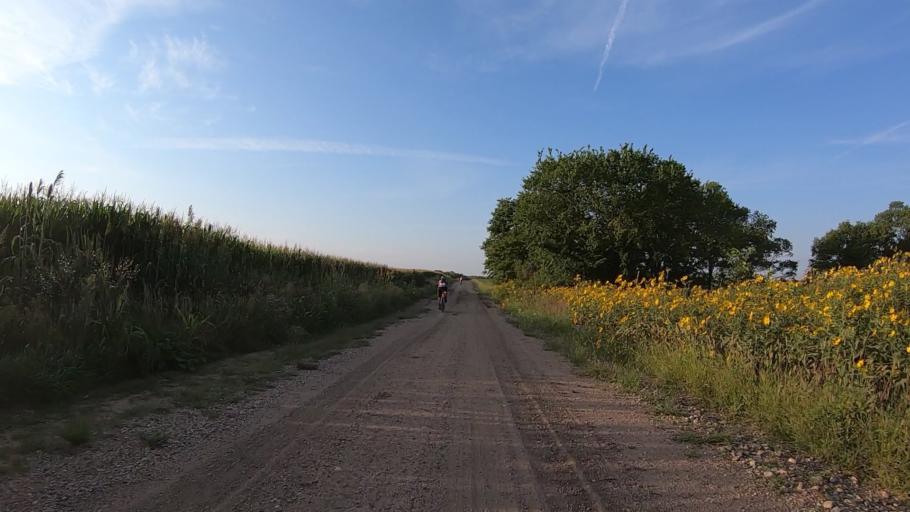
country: US
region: Kansas
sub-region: Marshall County
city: Blue Rapids
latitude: 39.7662
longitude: -96.7508
